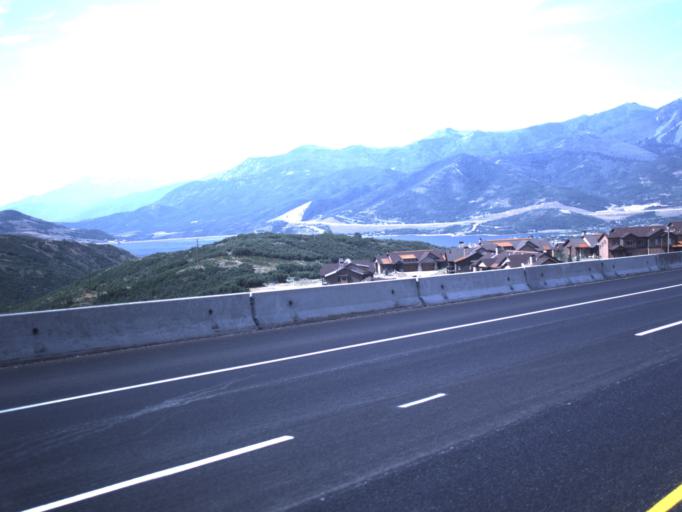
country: US
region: Utah
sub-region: Summit County
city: Kamas
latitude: 40.6338
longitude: -111.3845
